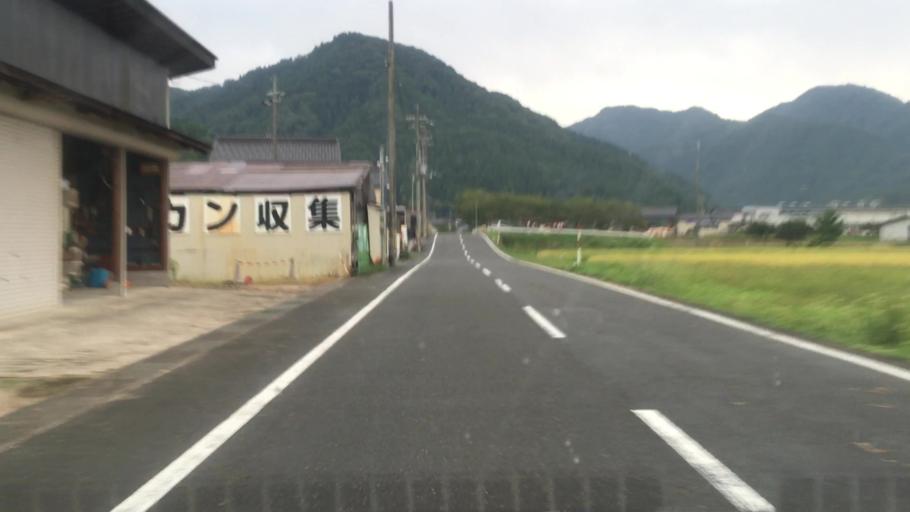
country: JP
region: Hyogo
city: Toyooka
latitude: 35.4578
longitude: 134.7354
